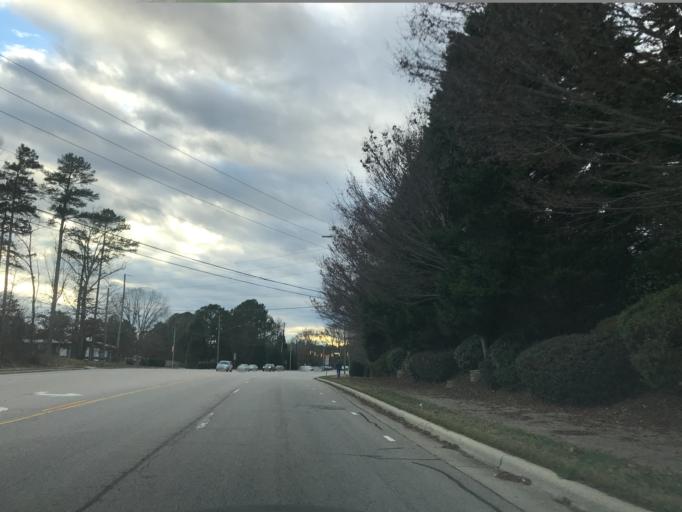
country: US
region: North Carolina
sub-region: Wake County
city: West Raleigh
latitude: 35.8716
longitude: -78.6616
